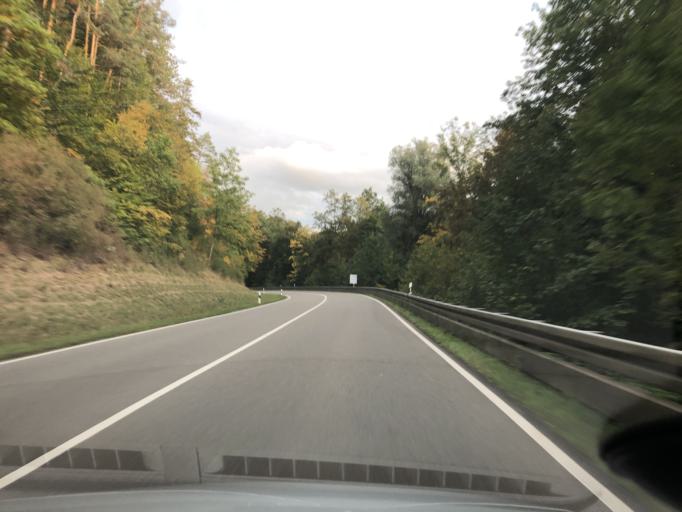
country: DE
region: Baden-Wuerttemberg
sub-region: Regierungsbezirk Stuttgart
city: Gerlingen
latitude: 48.7585
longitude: 9.0657
